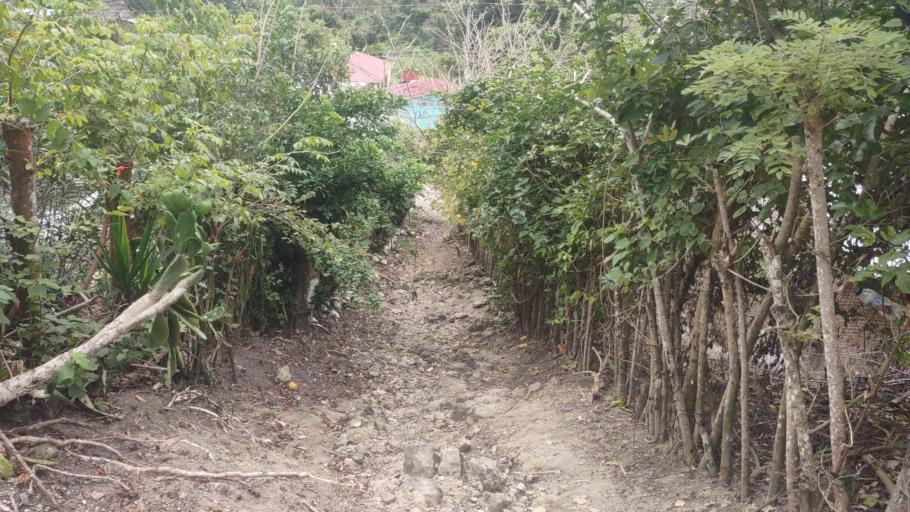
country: MX
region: Veracruz
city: Papantla de Olarte
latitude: 20.4351
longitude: -97.2630
